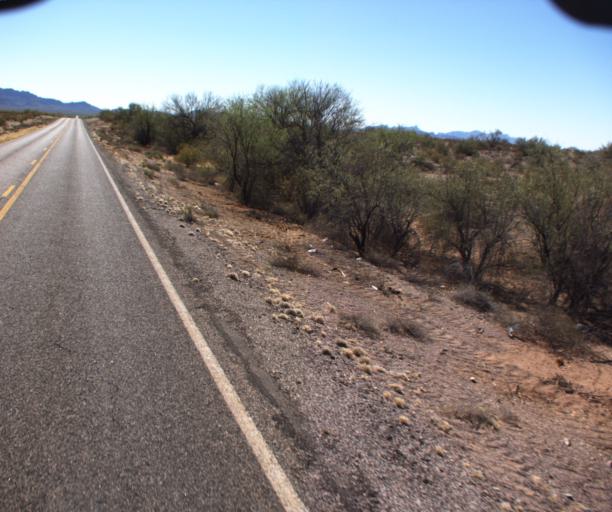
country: US
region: Arizona
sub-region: Pima County
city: Ajo
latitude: 32.3456
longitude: -112.8095
